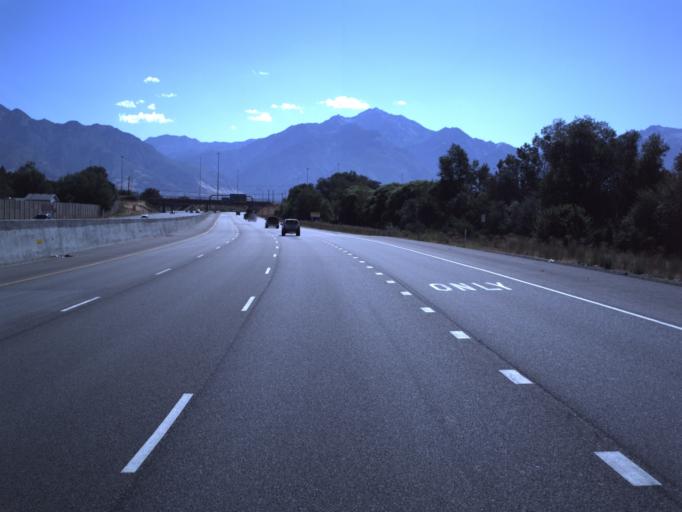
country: US
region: Utah
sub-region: Salt Lake County
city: Midvale
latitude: 40.6366
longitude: -111.9165
